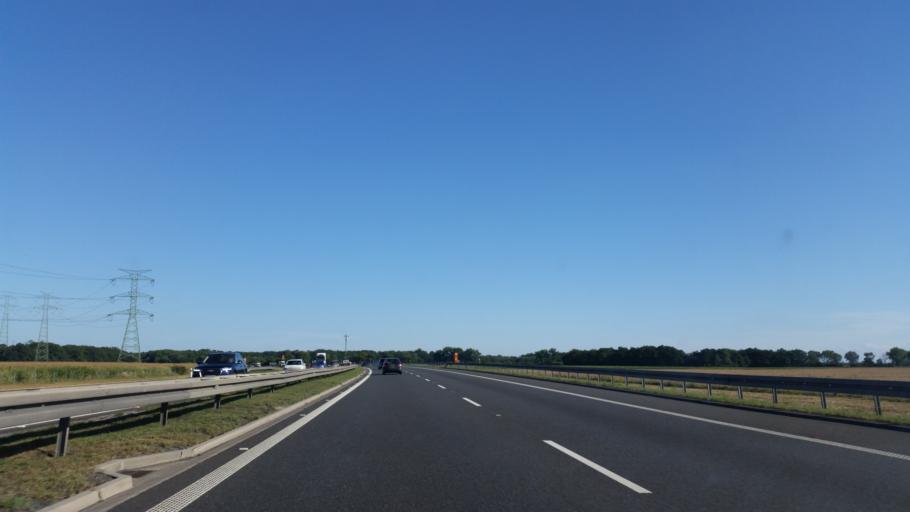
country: PL
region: Lower Silesian Voivodeship
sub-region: Powiat strzelinski
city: Wiazow
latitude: 50.8559
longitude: 17.2280
